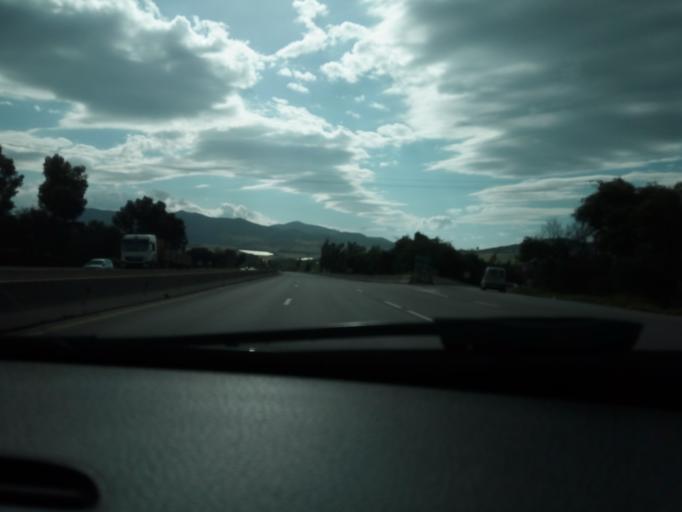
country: DZ
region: Tipaza
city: El Affroun
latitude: 36.4474
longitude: 2.5980
